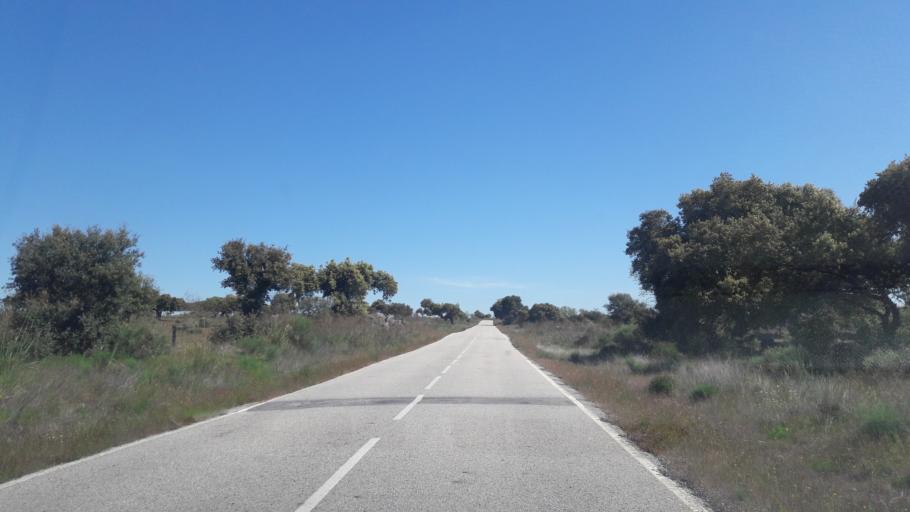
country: ES
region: Castille and Leon
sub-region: Provincia de Salamanca
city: Villarmuerto
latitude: 41.0388
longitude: -6.3929
